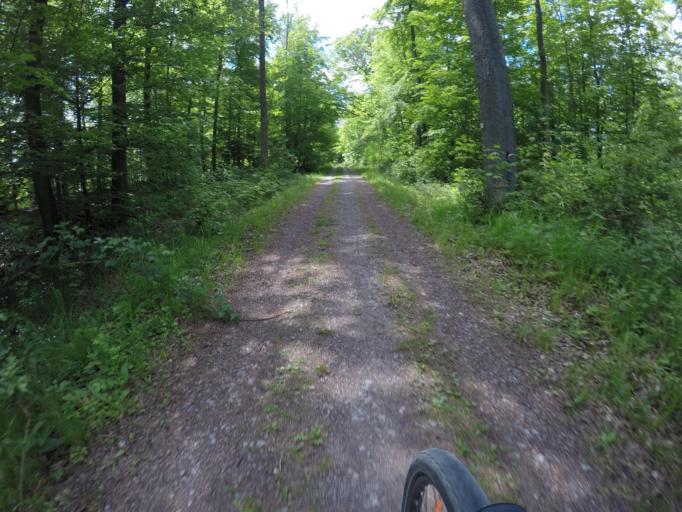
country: DE
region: Baden-Wuerttemberg
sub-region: Regierungsbezirk Stuttgart
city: Sindelfingen
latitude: 48.7405
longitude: 9.0546
